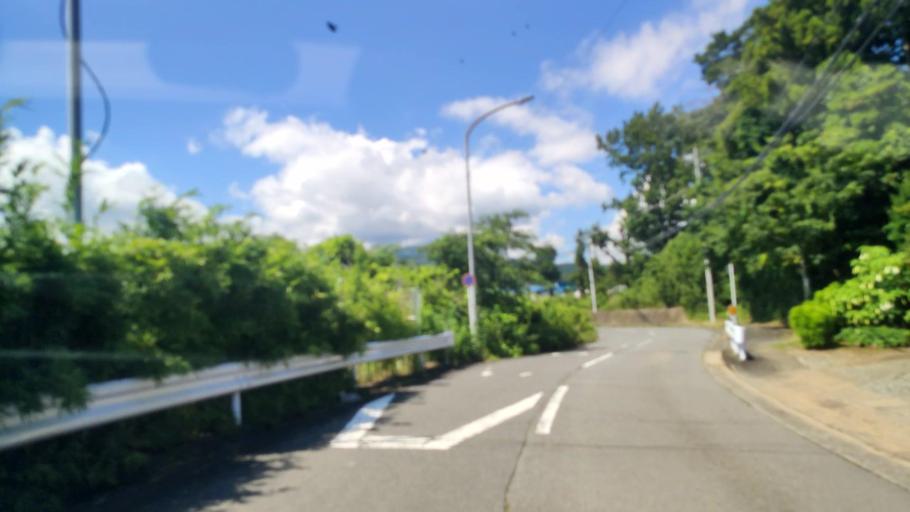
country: JP
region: Kanagawa
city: Odawara
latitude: 35.2533
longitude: 139.1376
